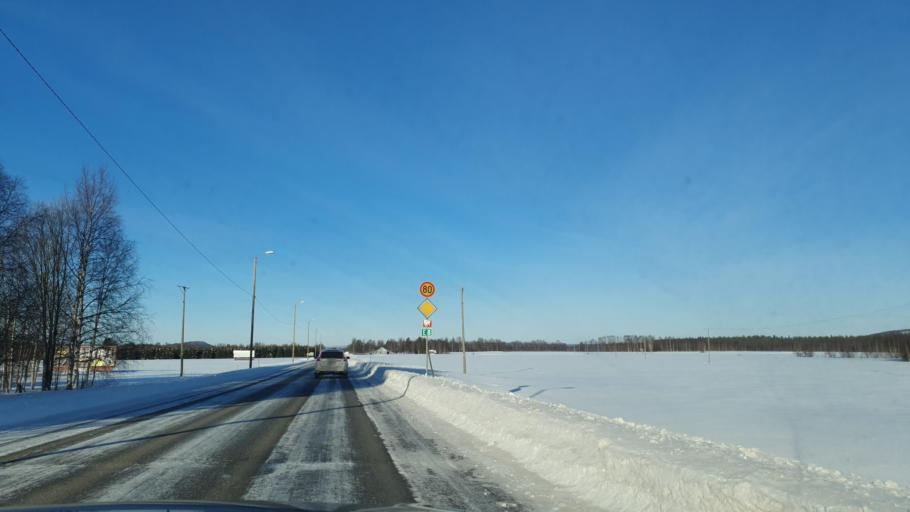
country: SE
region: Norrbotten
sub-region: Overtornea Kommun
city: OEvertornea
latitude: 66.4130
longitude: 23.6697
